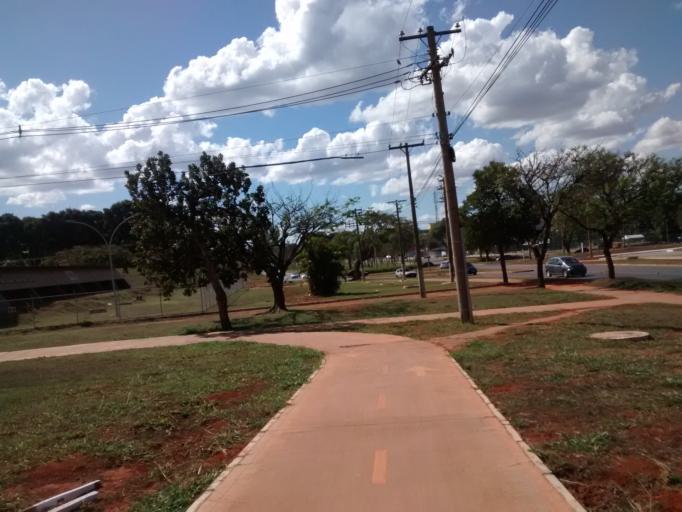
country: BR
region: Federal District
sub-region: Brasilia
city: Brasilia
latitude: -15.7845
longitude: -47.8913
